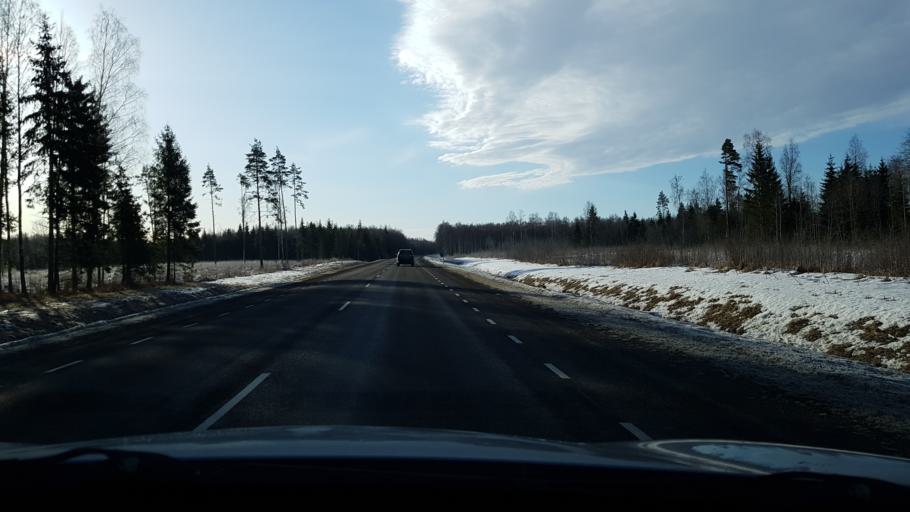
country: EE
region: Viljandimaa
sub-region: Vohma linn
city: Vohma
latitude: 58.6081
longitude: 25.5721
